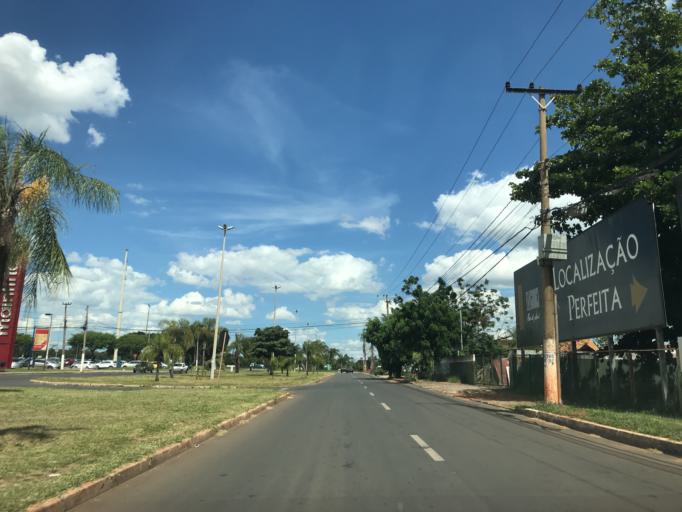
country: BR
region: Federal District
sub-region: Brasilia
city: Brasilia
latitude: -15.8279
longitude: -47.9536
